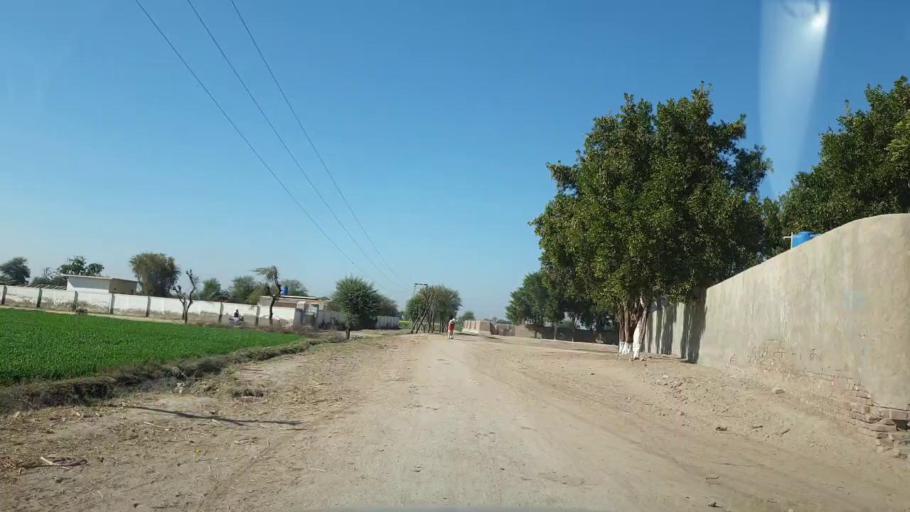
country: PK
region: Sindh
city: Jhol
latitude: 25.8065
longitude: 69.0326
